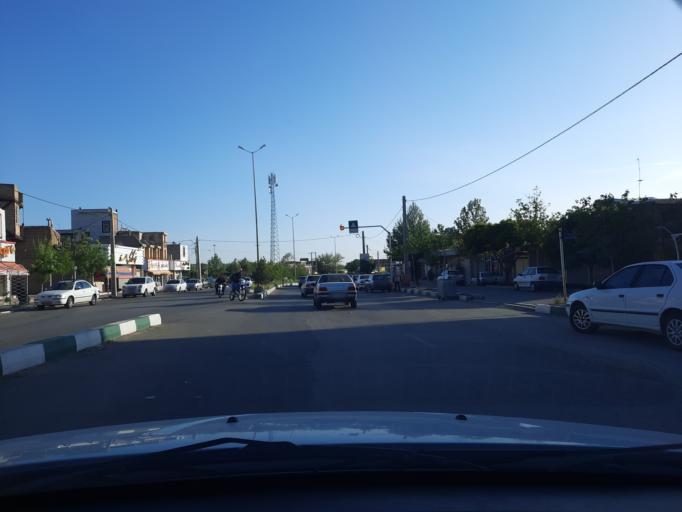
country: IR
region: Qazvin
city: Alvand
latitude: 36.2779
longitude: 50.1265
